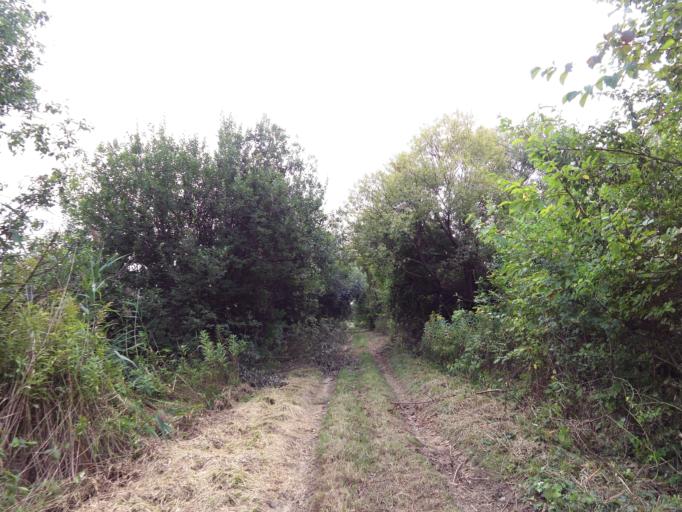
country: HU
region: Veszprem
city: Tapolca
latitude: 46.8318
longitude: 17.3705
